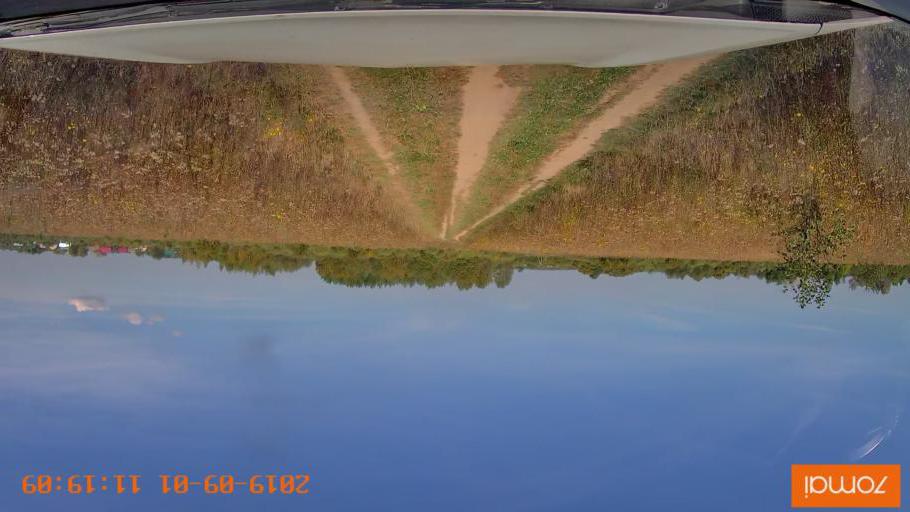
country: RU
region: Kaluga
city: Detchino
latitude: 54.8276
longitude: 36.3635
